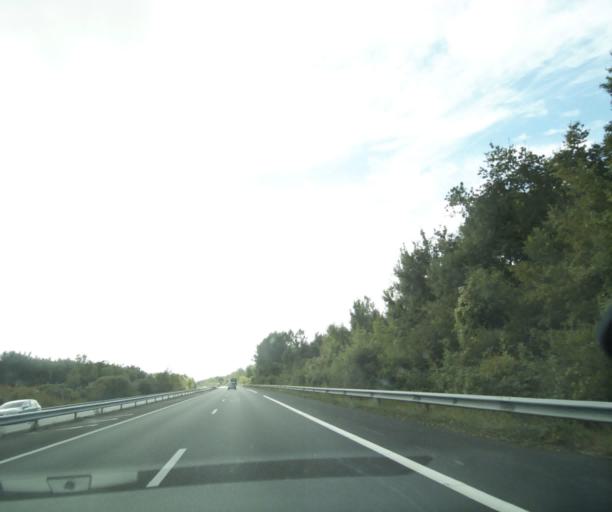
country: FR
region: Poitou-Charentes
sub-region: Departement de la Charente-Maritime
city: Thenac
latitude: 45.6488
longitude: -0.6321
